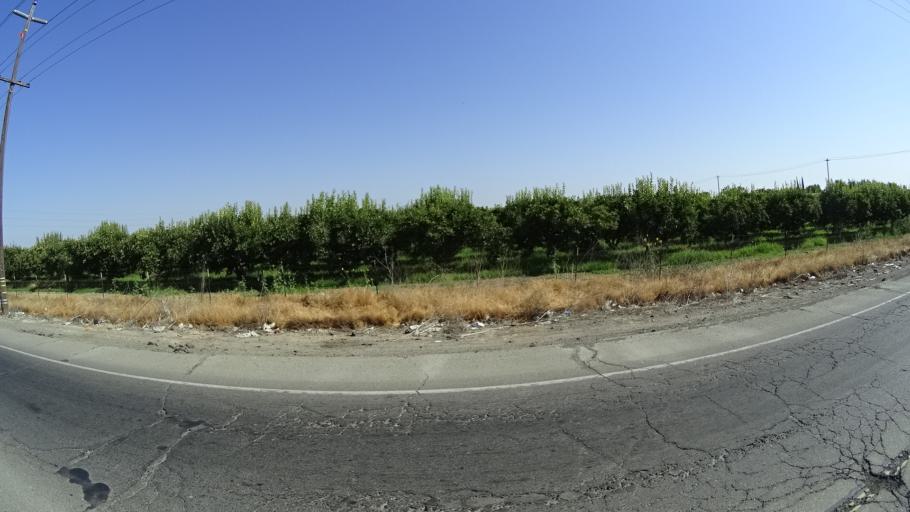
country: US
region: California
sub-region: Fresno County
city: West Park
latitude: 36.7068
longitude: -119.8192
